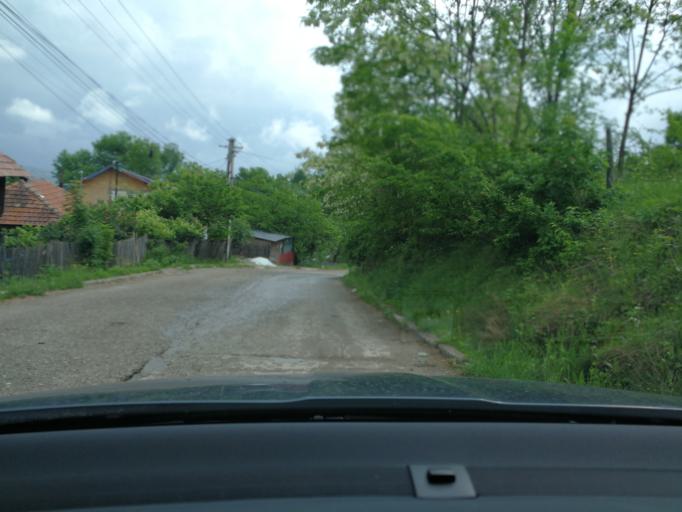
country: RO
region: Prahova
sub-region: Comuna Brebu
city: Pietriceaua
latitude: 45.2067
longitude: 25.8083
